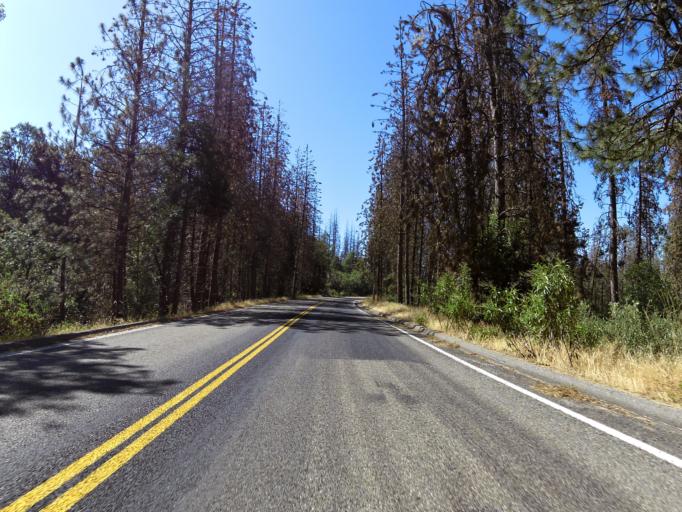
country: US
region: California
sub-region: Madera County
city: Oakhurst
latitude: 37.2907
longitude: -119.5204
